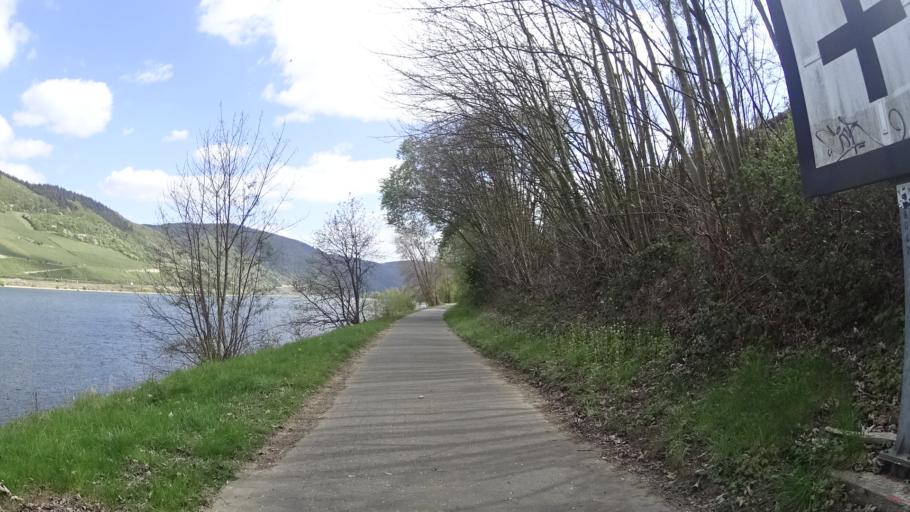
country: DE
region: Rheinland-Pfalz
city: Niederheimbach
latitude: 50.0224
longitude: 7.8261
